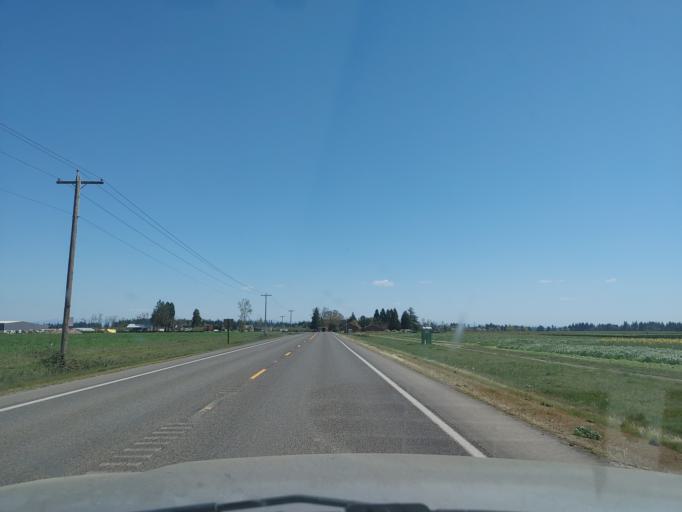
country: US
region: Oregon
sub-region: Yamhill County
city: Newberg
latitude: 45.2365
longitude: -122.9165
